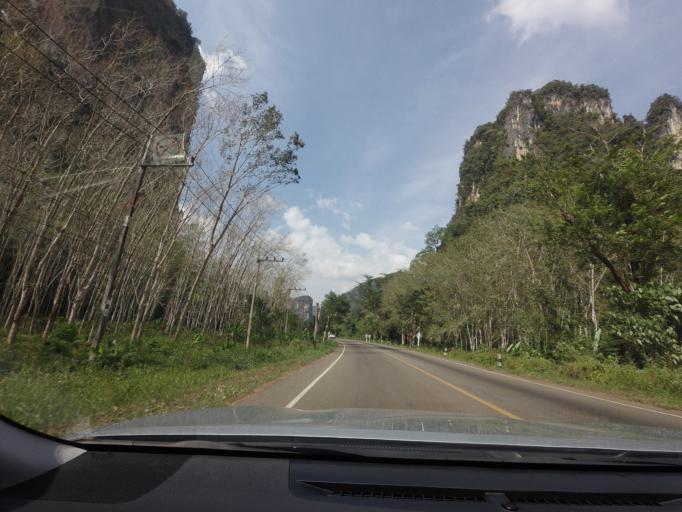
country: TH
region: Phangnga
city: Ban Ao Nang
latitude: 8.1404
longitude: 98.8119
